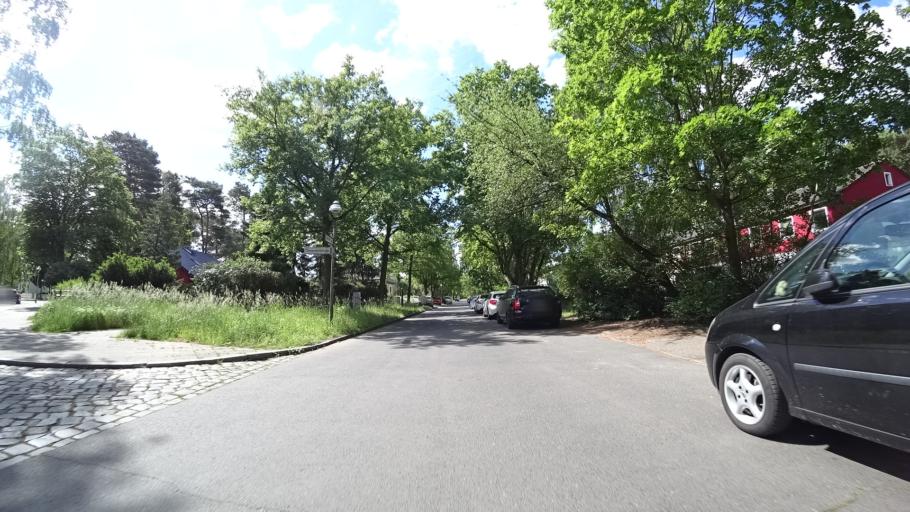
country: DE
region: Berlin
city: Lichtenrade
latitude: 52.3940
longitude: 13.3815
